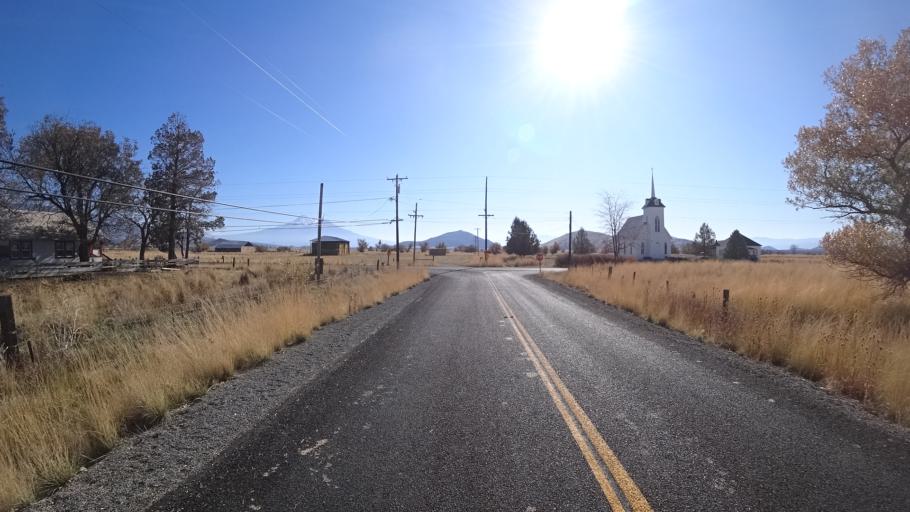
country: US
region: California
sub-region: Siskiyou County
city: Montague
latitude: 41.7119
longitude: -122.3892
